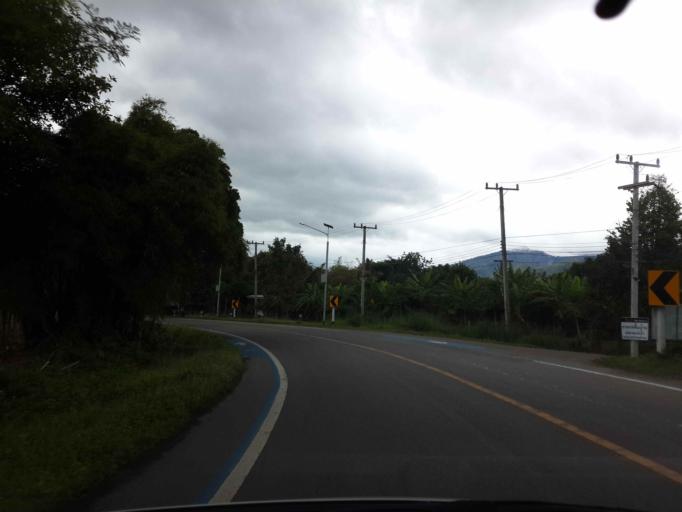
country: TH
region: Ratchaburi
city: Suan Phueng
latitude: 13.6220
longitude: 99.2211
